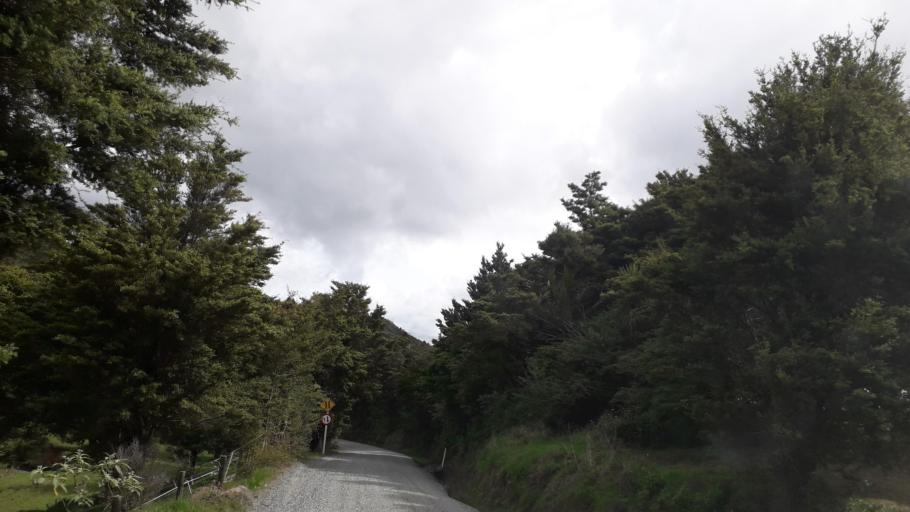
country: NZ
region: Northland
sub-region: Far North District
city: Kerikeri
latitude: -35.1305
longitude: 173.7398
